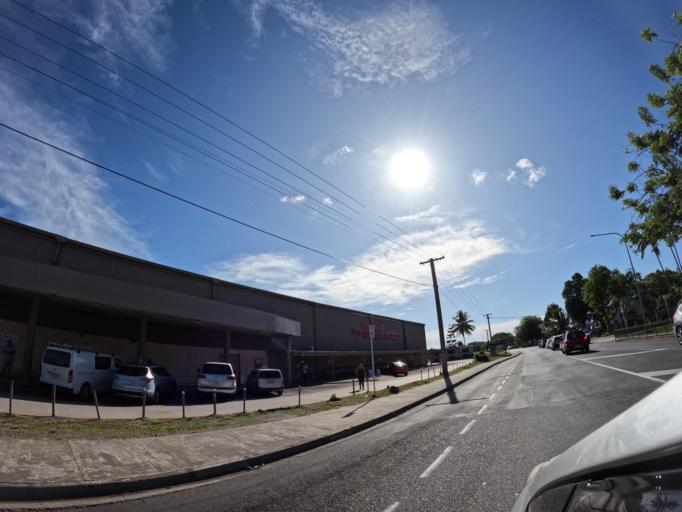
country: FJ
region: Central
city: Suva
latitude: -18.1476
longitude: 178.4470
